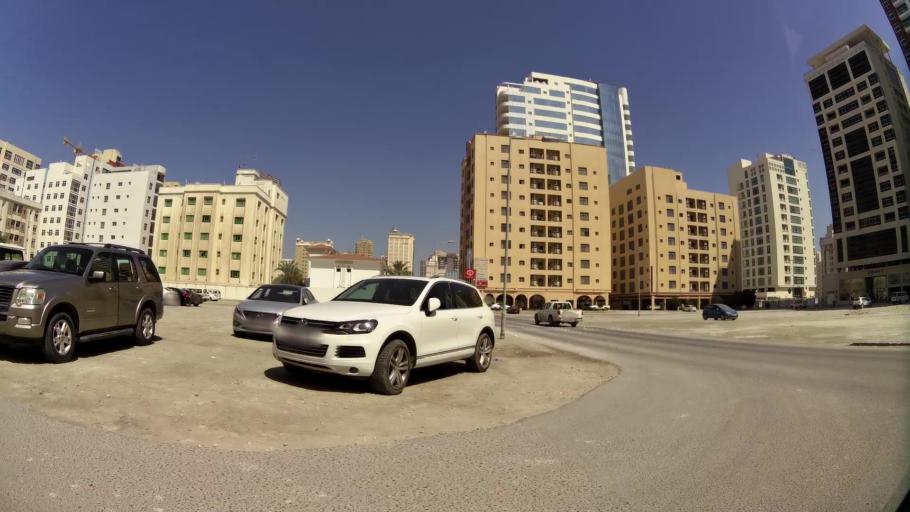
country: BH
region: Manama
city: Manama
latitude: 26.2135
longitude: 50.6052
